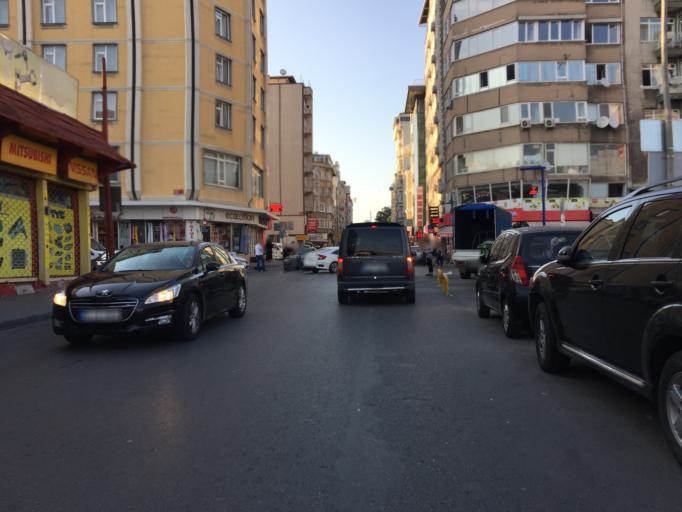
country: TR
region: Istanbul
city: Istanbul
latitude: 41.0067
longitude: 28.9502
